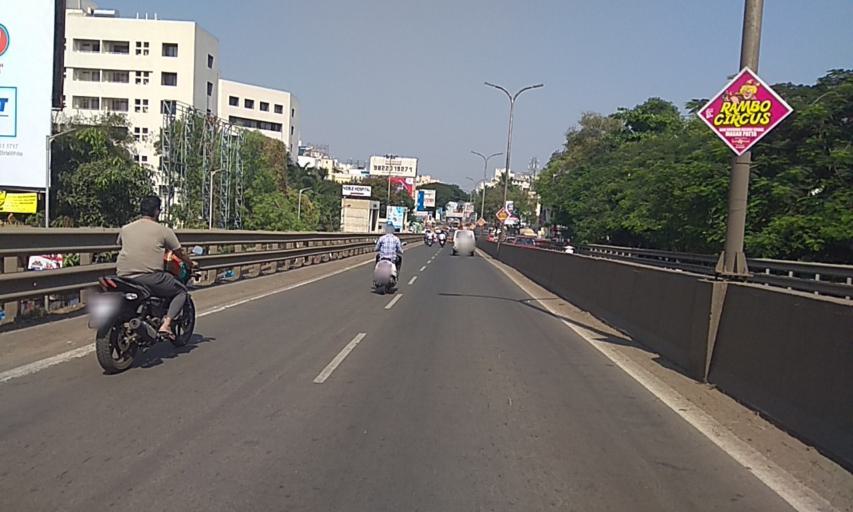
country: IN
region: Maharashtra
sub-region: Pune Division
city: Pune
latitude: 18.5040
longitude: 73.9276
